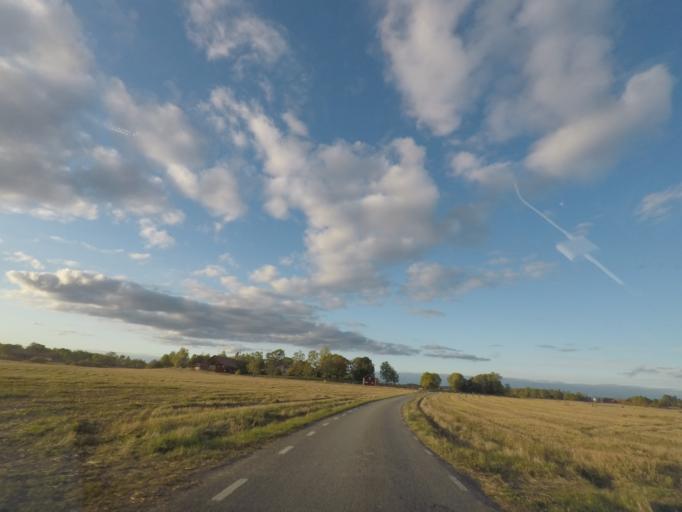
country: SE
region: Vaestmanland
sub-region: Kungsors Kommun
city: Kungsoer
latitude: 59.5153
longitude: 16.1125
